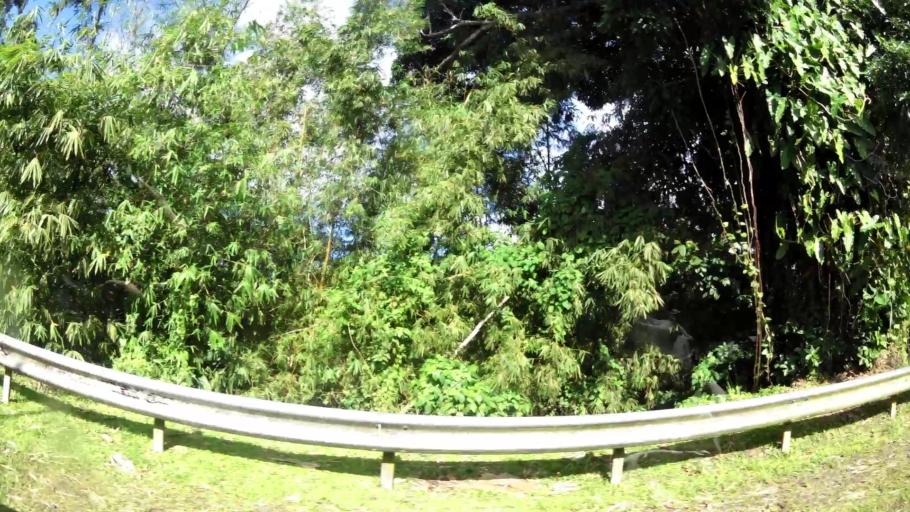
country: MQ
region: Martinique
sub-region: Martinique
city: Saint-Joseph
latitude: 14.6674
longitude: -61.0886
